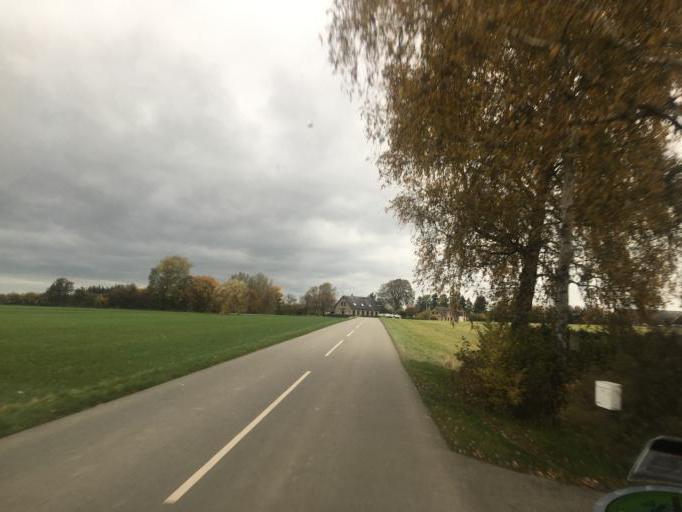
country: DK
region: Zealand
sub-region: Koge Kommune
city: Bjaeverskov
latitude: 55.4226
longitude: 11.9818
